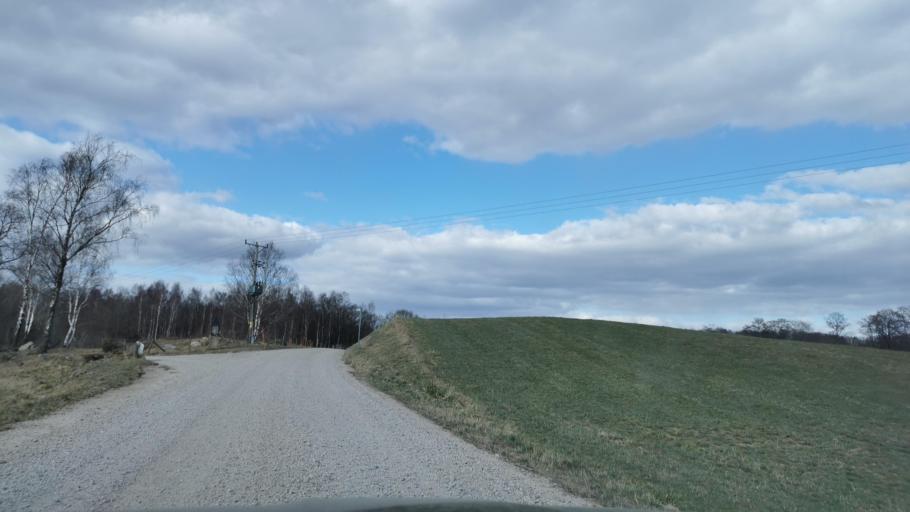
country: SE
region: Skane
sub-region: Sjobo Kommun
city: Sjoebo
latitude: 55.7417
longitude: 13.8370
